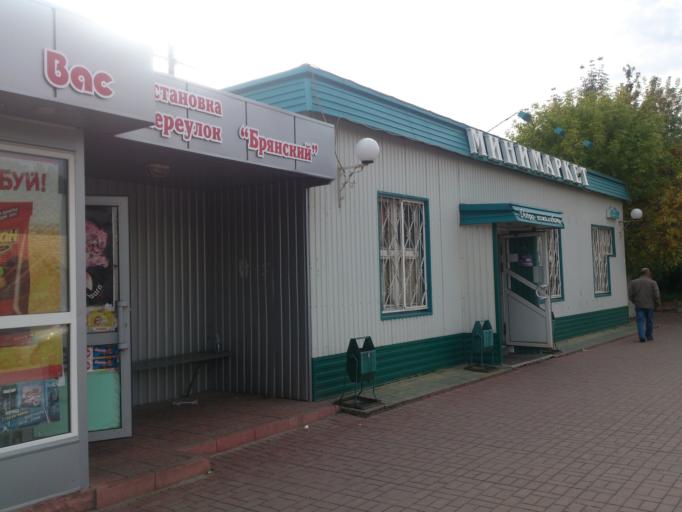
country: RU
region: Ulyanovsk
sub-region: Ulyanovskiy Rayon
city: Ulyanovsk
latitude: 54.2824
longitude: 48.3081
